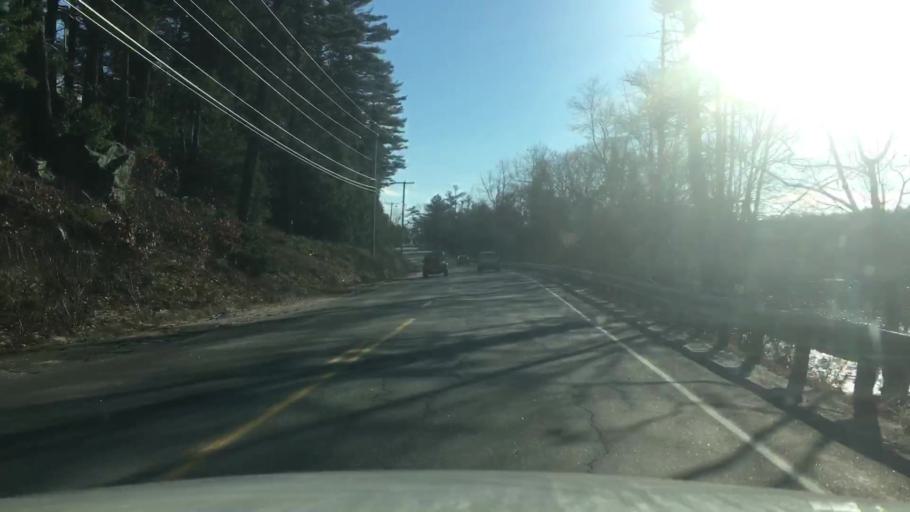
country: US
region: Maine
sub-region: Cumberland County
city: Brunswick
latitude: 43.8687
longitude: -69.9139
